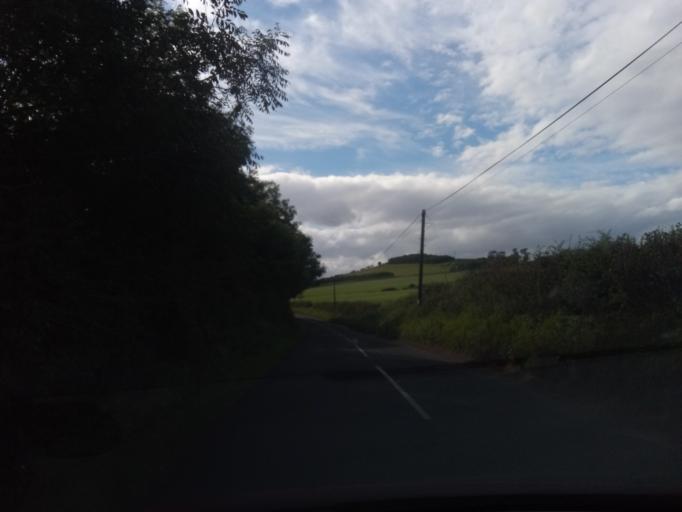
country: GB
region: Scotland
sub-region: The Scottish Borders
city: Coldstream
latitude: 55.5955
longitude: -2.2063
